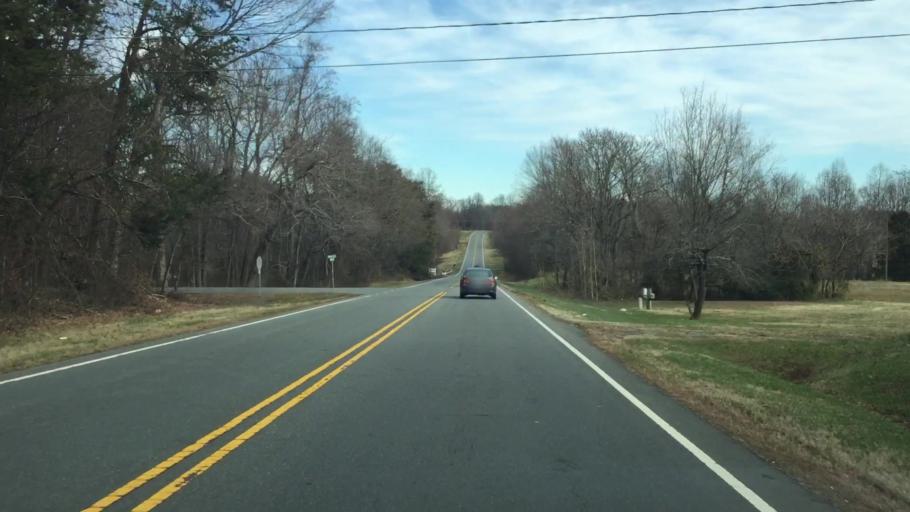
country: US
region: North Carolina
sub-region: Forsyth County
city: Walkertown
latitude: 36.1790
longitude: -80.1218
